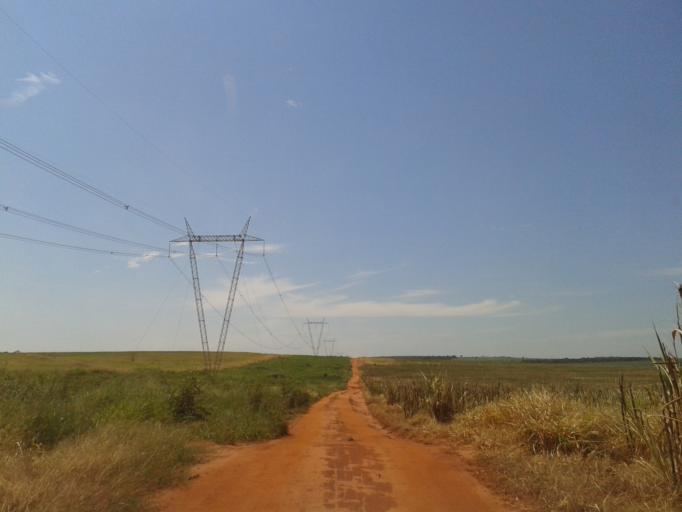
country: BR
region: Minas Gerais
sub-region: Santa Vitoria
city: Santa Vitoria
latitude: -19.0793
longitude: -50.4577
